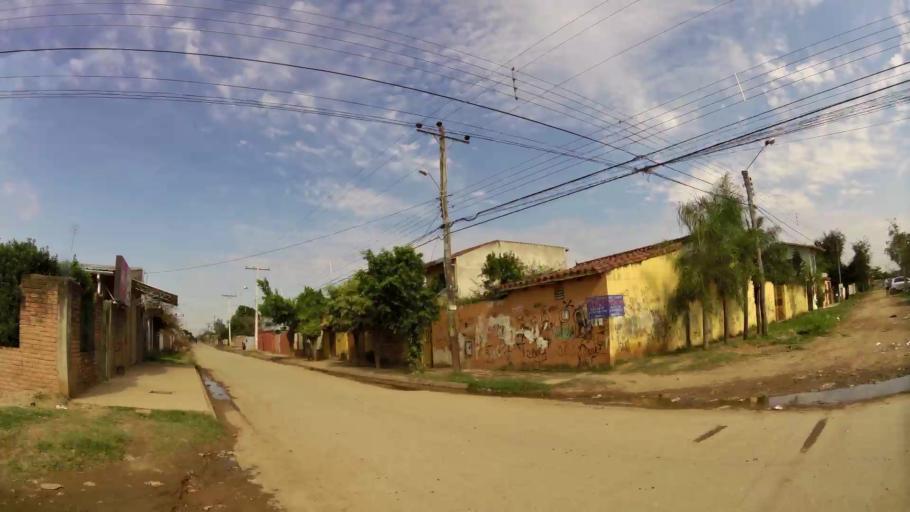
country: BO
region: Santa Cruz
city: Santa Cruz de la Sierra
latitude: -17.7227
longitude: -63.1374
